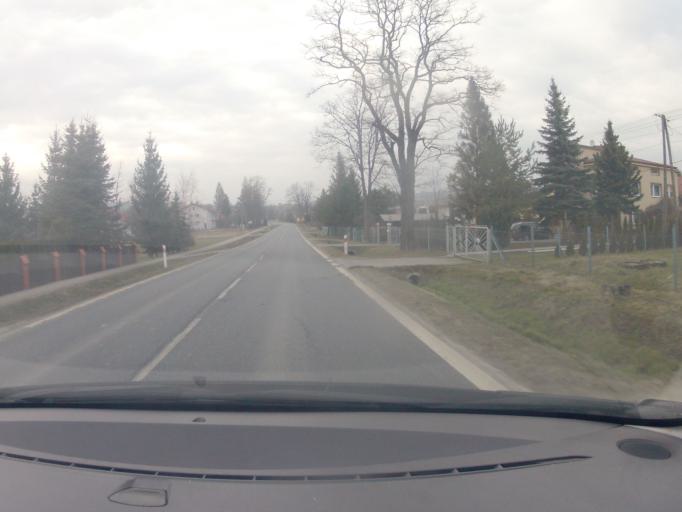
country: PL
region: Subcarpathian Voivodeship
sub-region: Powiat krosnienski
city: Dukla
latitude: 49.5589
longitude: 21.6260
